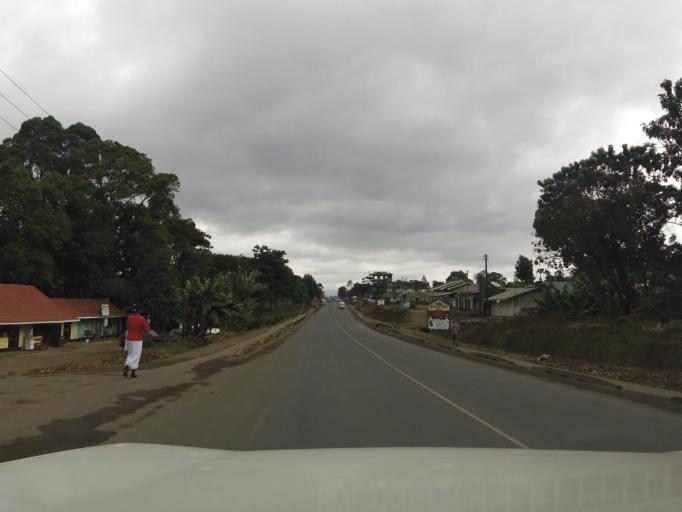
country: TZ
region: Arusha
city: Arusha
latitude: -3.3667
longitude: 36.7103
